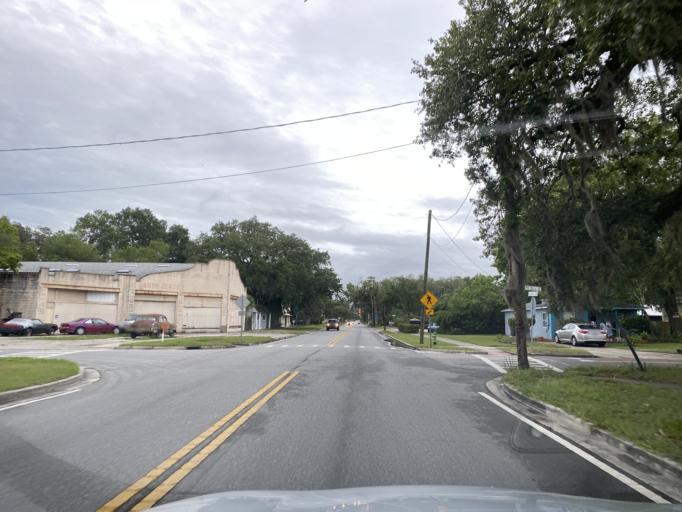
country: US
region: Florida
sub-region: Seminole County
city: Sanford
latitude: 28.8038
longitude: -81.2649
